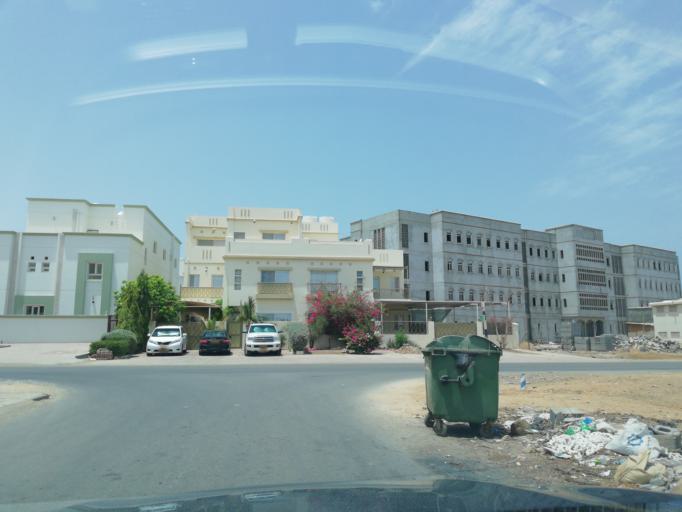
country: OM
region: Muhafazat Masqat
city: As Sib al Jadidah
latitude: 23.6253
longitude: 58.2533
